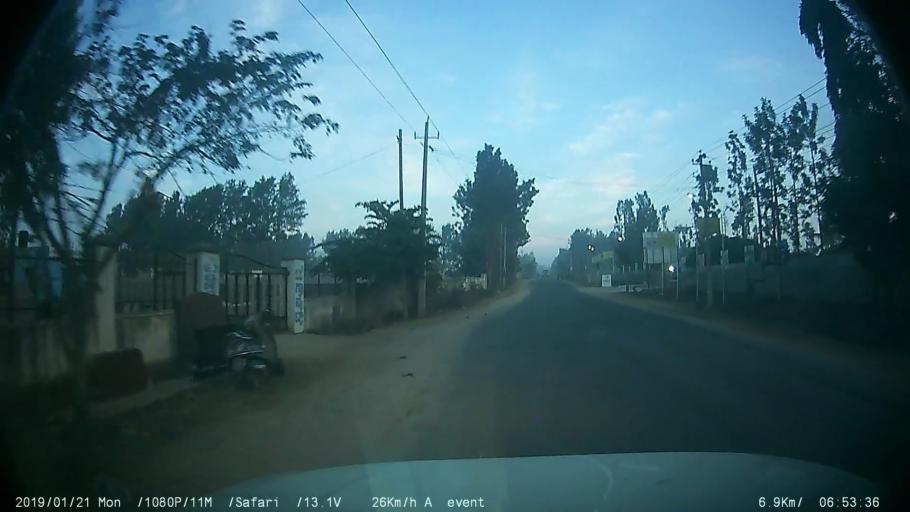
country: IN
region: Karnataka
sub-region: Bangalore Urban
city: Anekal
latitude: 12.8219
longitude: 77.6226
